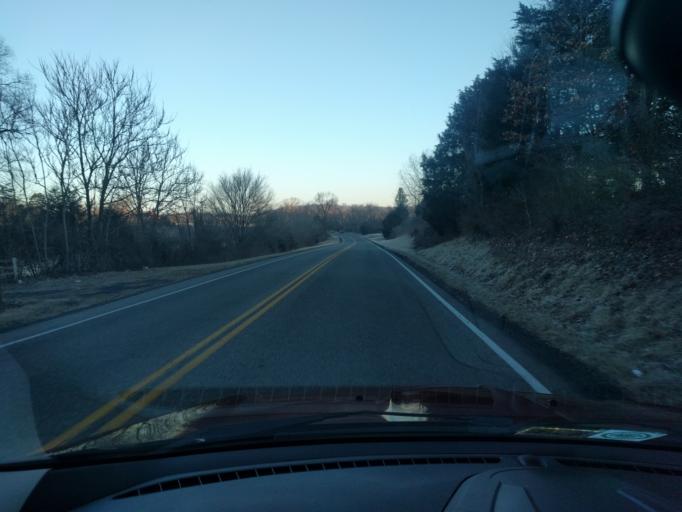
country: US
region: Virginia
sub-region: Augusta County
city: Weyers Cave
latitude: 38.2978
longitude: -78.9345
